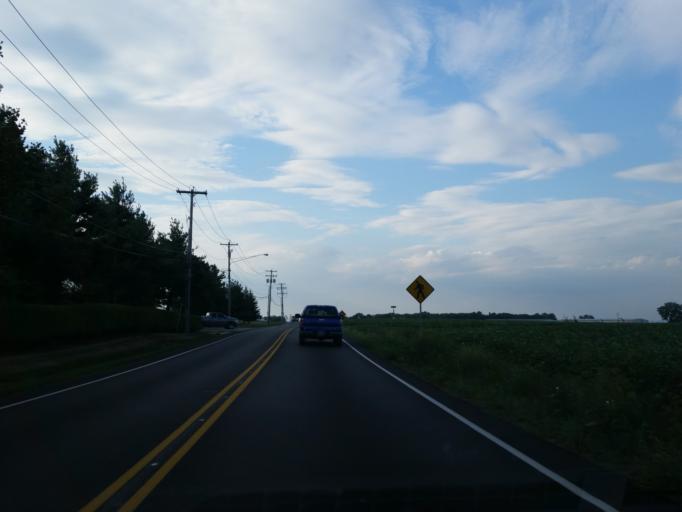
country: US
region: Pennsylvania
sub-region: Lebanon County
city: Campbelltown
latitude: 40.2822
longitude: -76.5727
